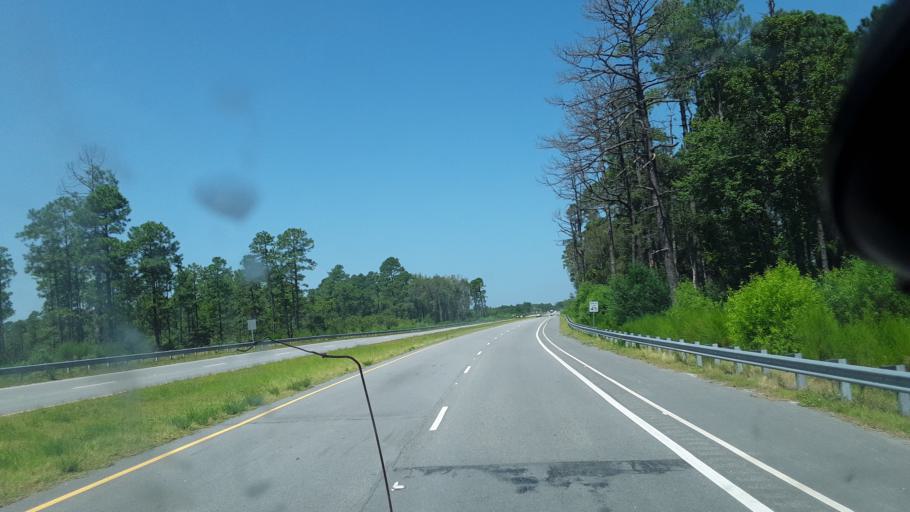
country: US
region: South Carolina
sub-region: Horry County
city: Forestbrook
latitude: 33.8070
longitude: -78.8938
